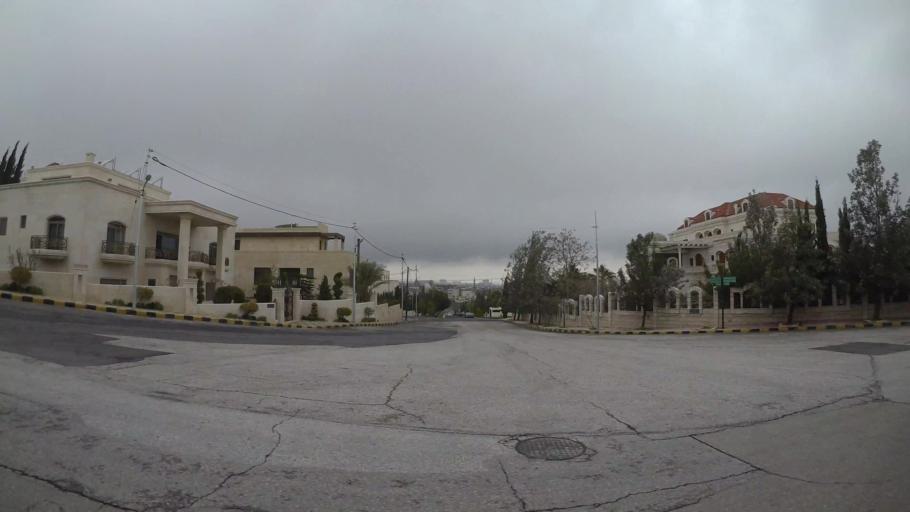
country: JO
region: Amman
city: Al Bunayyat ash Shamaliyah
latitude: 31.9376
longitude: 35.8840
